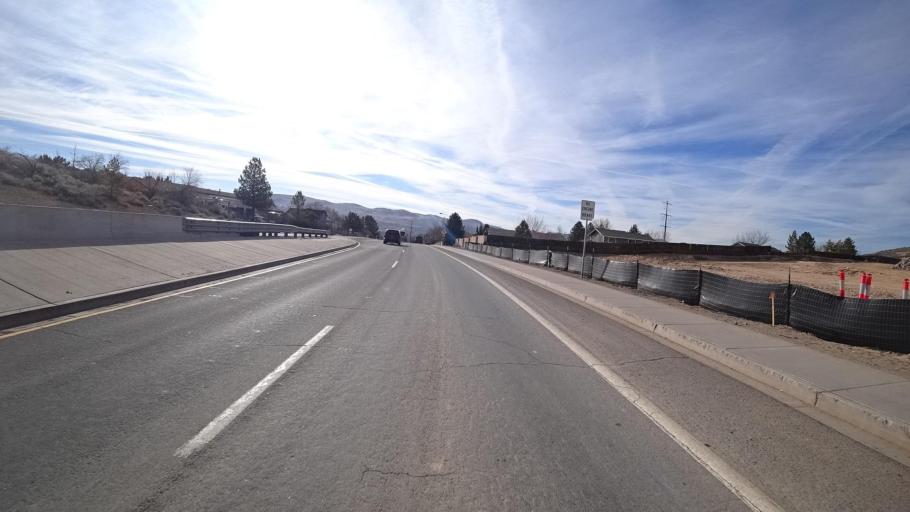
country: US
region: Nevada
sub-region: Washoe County
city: Sparks
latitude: 39.5712
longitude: -119.7201
